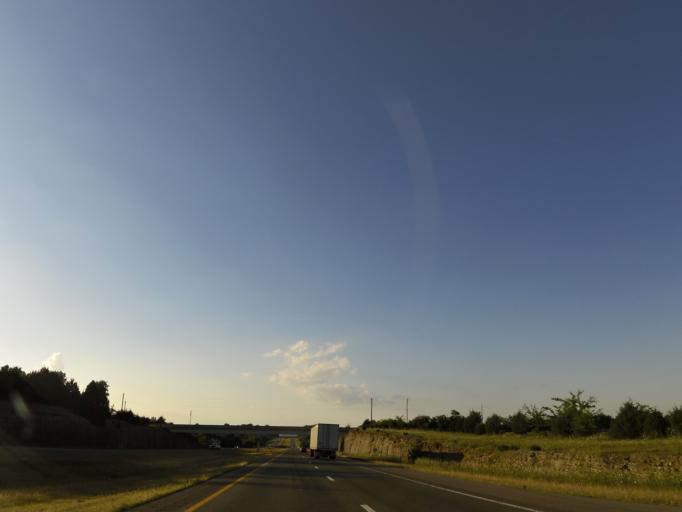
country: US
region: Tennessee
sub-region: Rutherford County
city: Smyrna
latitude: 36.0158
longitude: -86.4276
